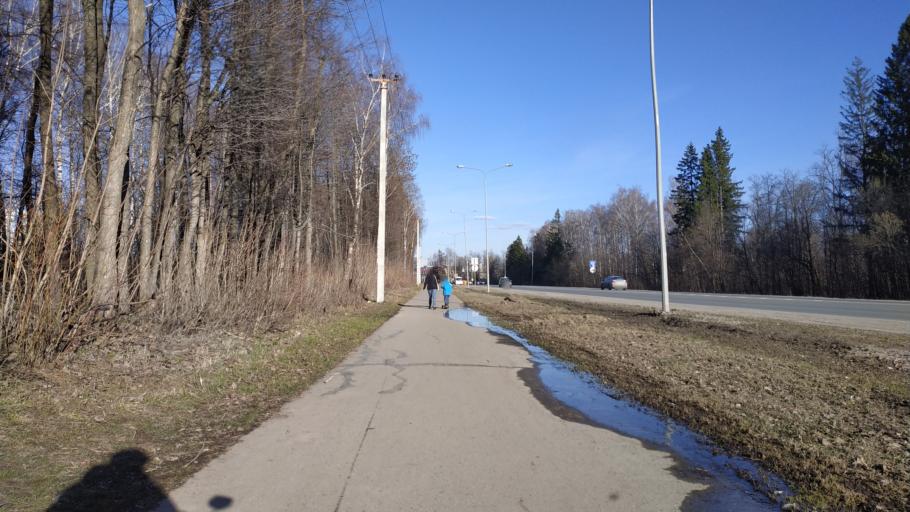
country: RU
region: Chuvashia
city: Novyye Lapsary
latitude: 56.1303
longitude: 47.1544
